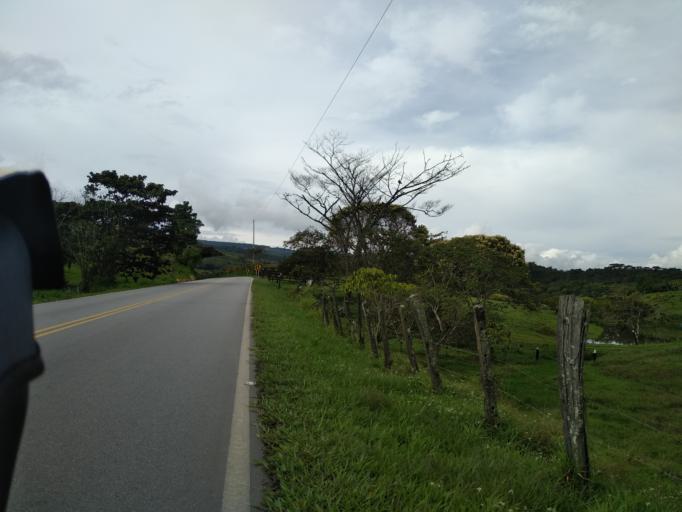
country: CO
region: Santander
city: Suaita
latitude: 6.1128
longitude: -73.3673
